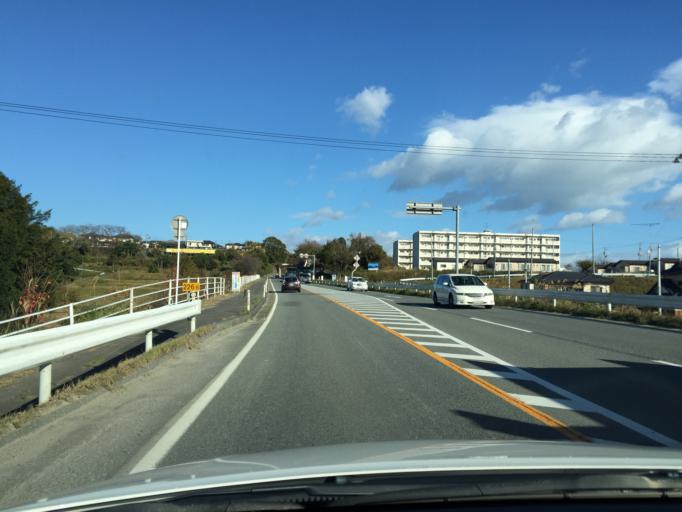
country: JP
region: Fukushima
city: Iwaki
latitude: 37.2077
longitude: 140.9933
